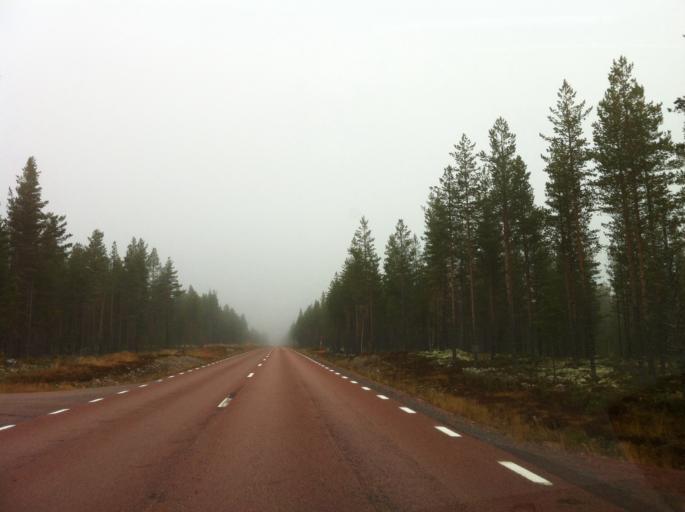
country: NO
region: Hedmark
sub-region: Trysil
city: Innbygda
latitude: 61.6782
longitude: 13.1666
